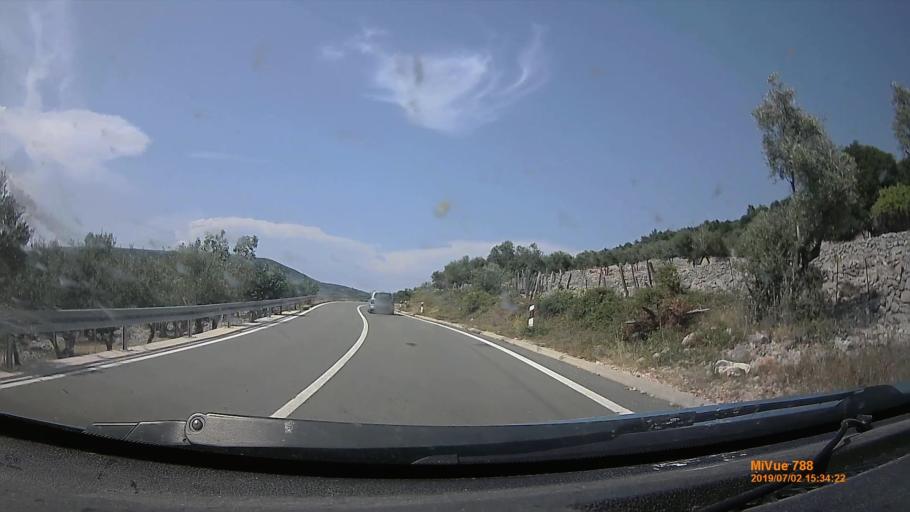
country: HR
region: Primorsko-Goranska
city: Cres
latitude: 44.9664
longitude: 14.4127
